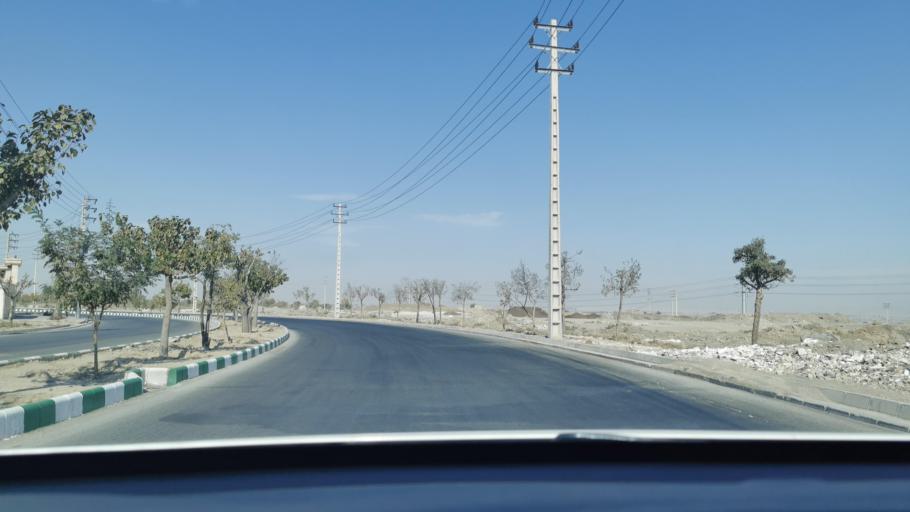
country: IR
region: Razavi Khorasan
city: Mashhad
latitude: 36.3462
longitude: 59.6115
